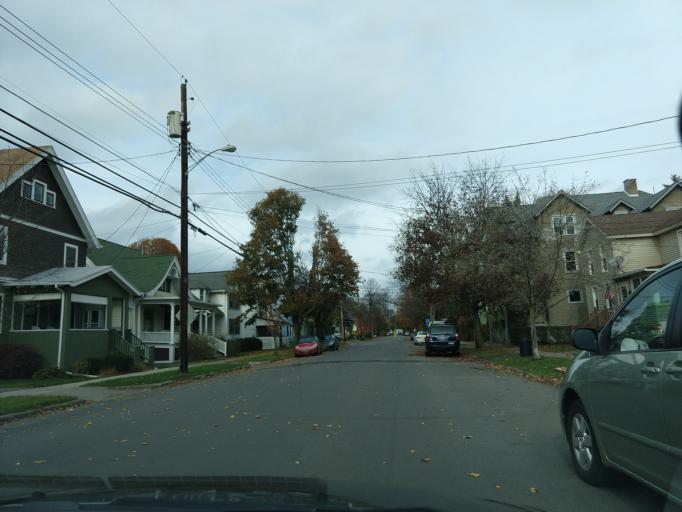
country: US
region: New York
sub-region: Tompkins County
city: Ithaca
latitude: 42.4488
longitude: -76.4974
